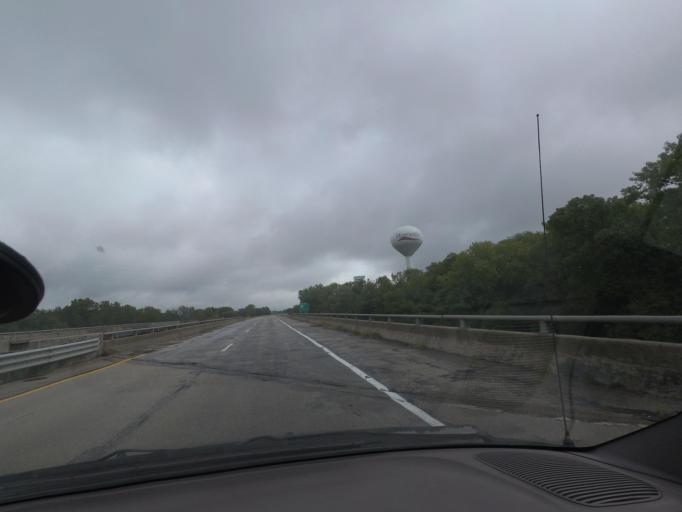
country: US
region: Illinois
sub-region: Piatt County
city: Monticello
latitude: 40.0489
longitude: -88.5748
